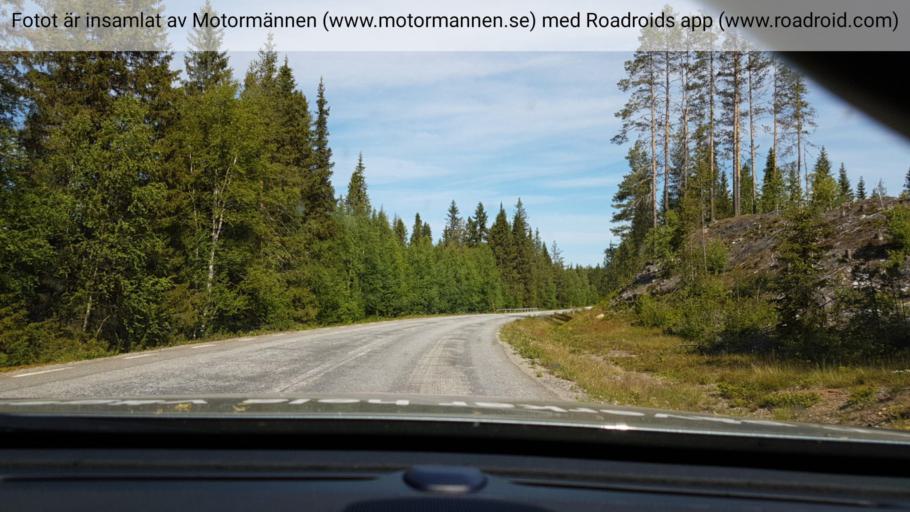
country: SE
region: Vaesterbotten
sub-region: Vilhelmina Kommun
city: Sjoberg
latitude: 64.6157
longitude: 15.8442
